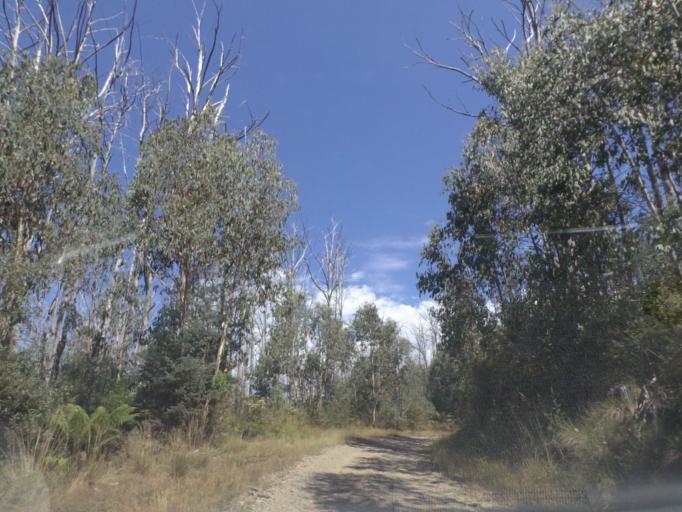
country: AU
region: Victoria
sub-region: Murrindindi
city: Alexandra
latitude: -37.4502
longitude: 145.8065
